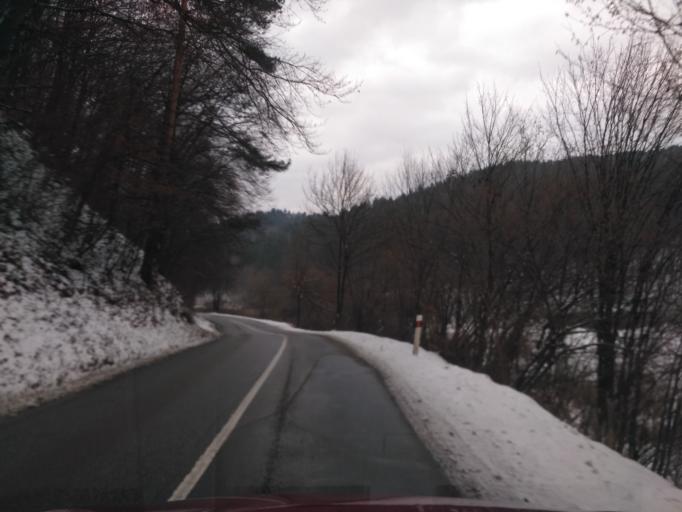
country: SK
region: Presovsky
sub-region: Okres Presov
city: Presov
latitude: 48.9625
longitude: 21.1010
